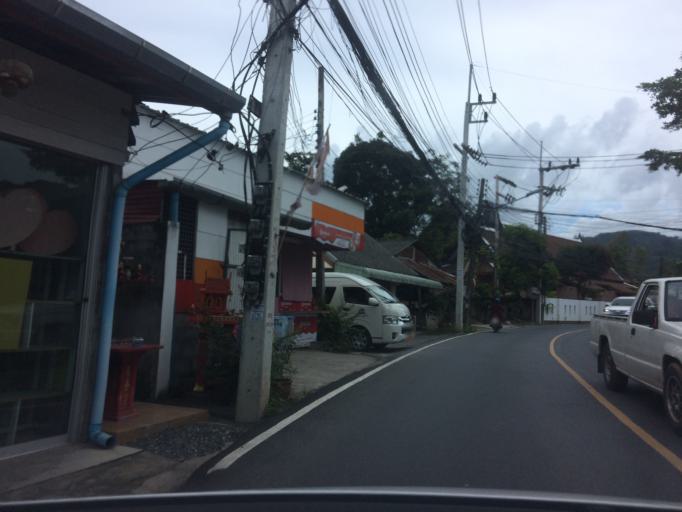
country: TH
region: Phuket
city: Mueang Phuket
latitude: 7.8637
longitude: 98.3586
